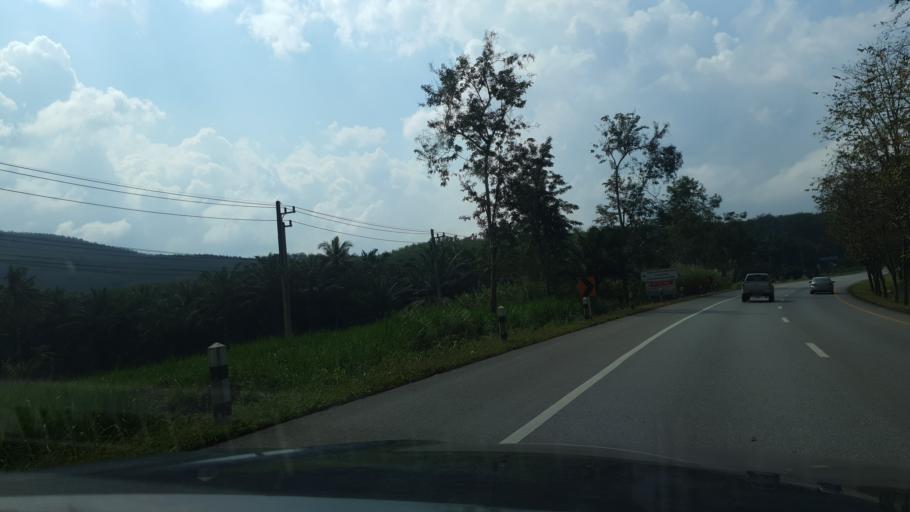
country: TH
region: Chumphon
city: Pathio
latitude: 10.8911
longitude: 99.2683
